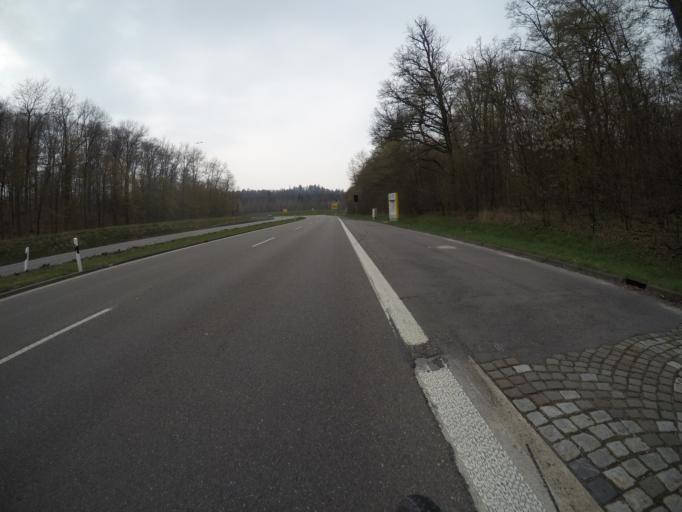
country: DE
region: Baden-Wuerttemberg
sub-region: Regierungsbezirk Stuttgart
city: Sindelfingen
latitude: 48.6976
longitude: 9.0308
